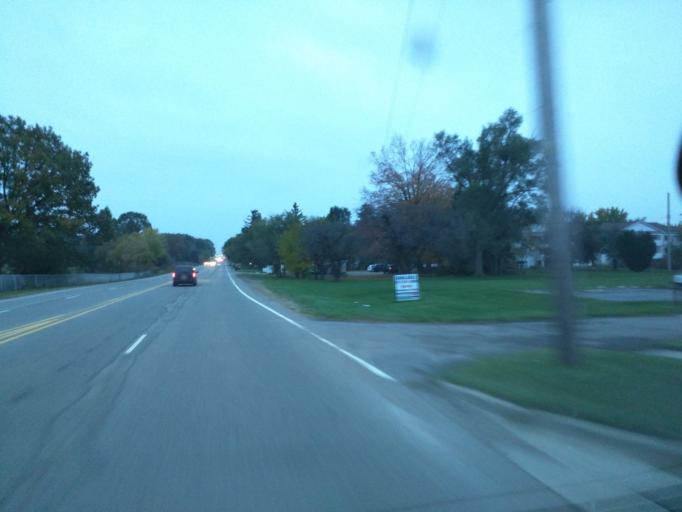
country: US
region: Michigan
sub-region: Ingham County
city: Edgemont Park
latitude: 42.7396
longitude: -84.6030
